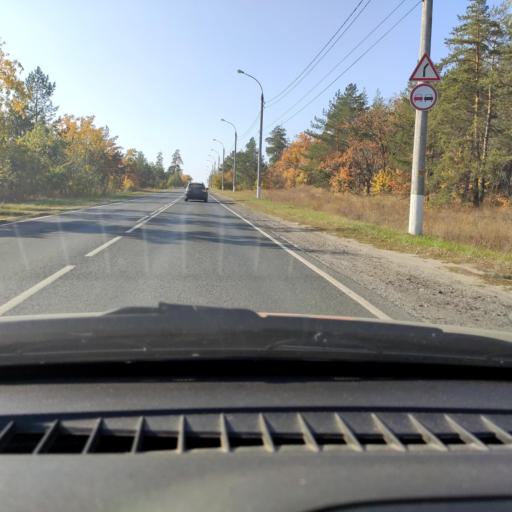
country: RU
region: Samara
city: Tol'yatti
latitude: 53.4752
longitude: 49.4168
